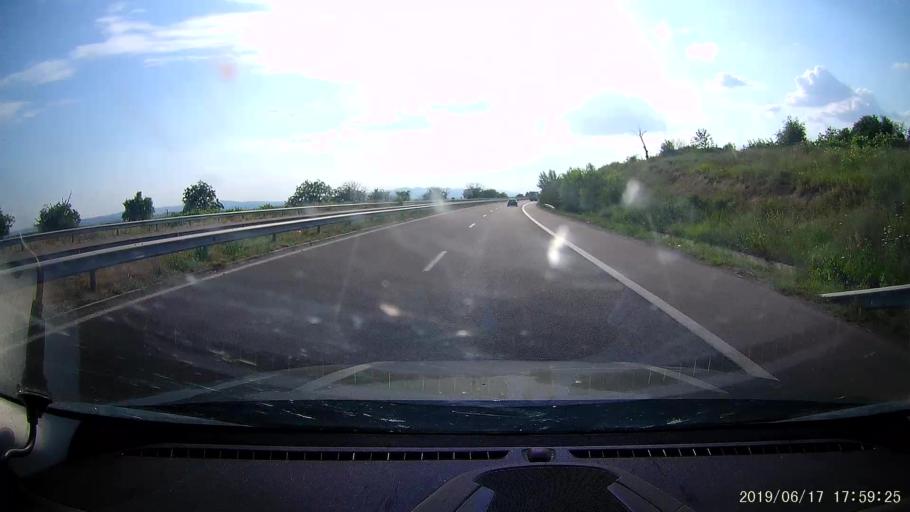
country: BG
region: Khaskovo
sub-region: Obshtina Svilengrad
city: Svilengrad
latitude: 41.7245
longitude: 26.2985
